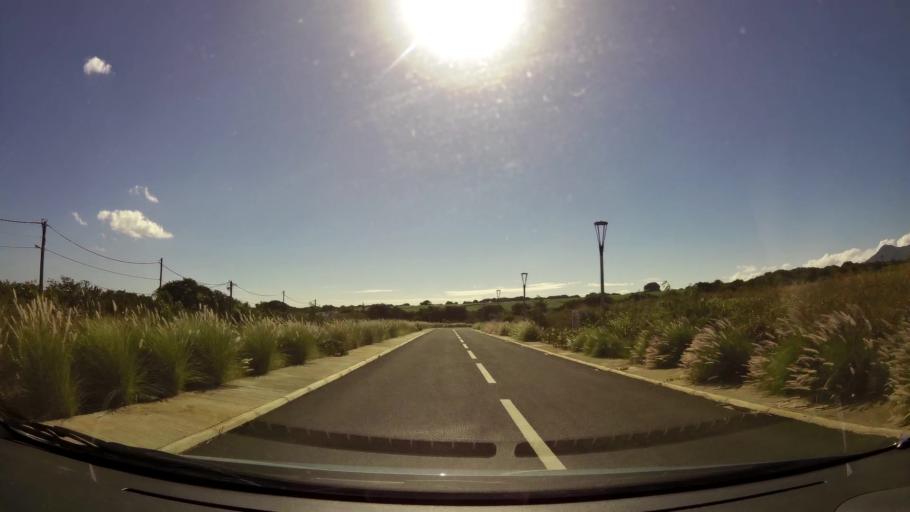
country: MU
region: Black River
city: Flic en Flac
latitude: -20.2643
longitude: 57.3794
